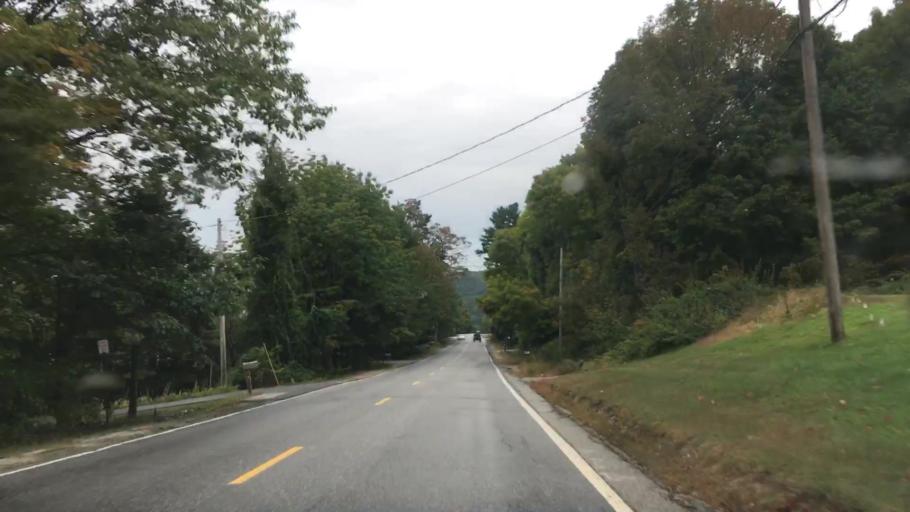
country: US
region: Maine
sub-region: Cumberland County
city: Raymond
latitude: 43.9409
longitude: -70.4532
